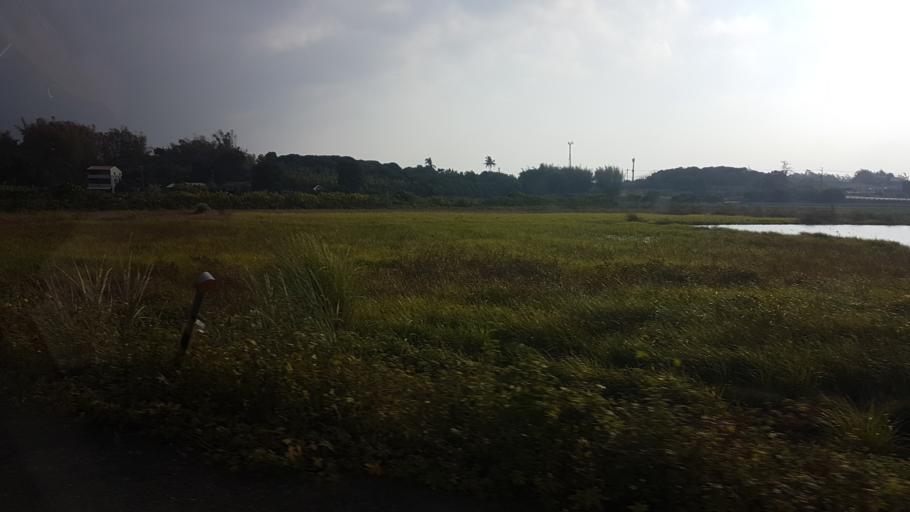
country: TW
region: Taiwan
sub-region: Chiayi
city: Jiayi Shi
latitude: 23.3877
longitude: 120.4356
